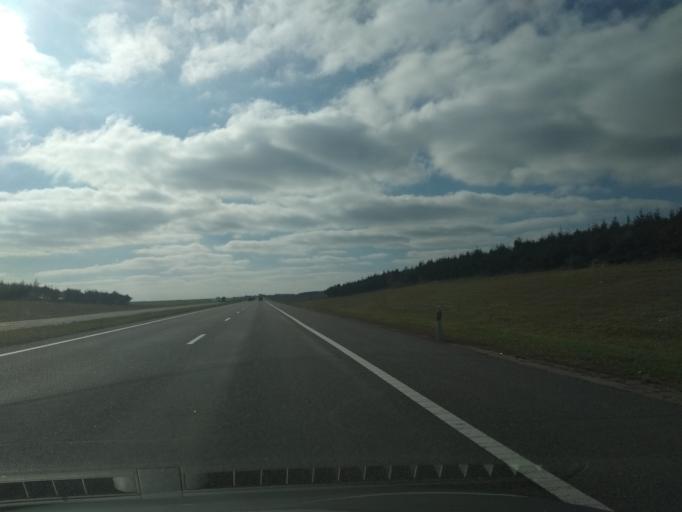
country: BY
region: Grodnenskaya
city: Mir
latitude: 53.4369
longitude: 26.5884
